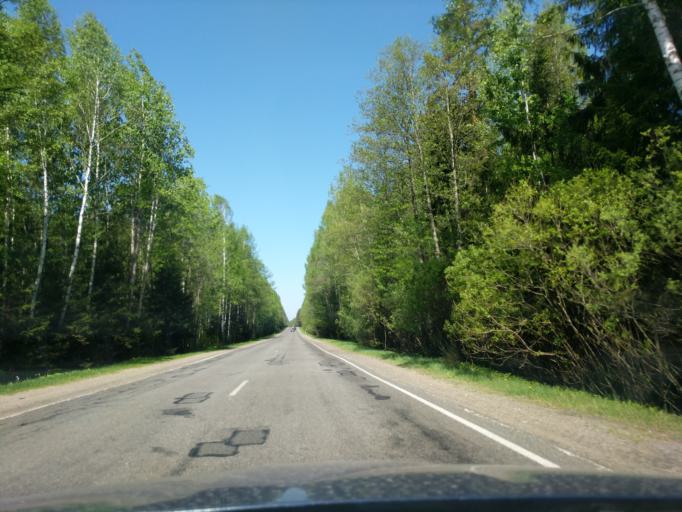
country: BY
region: Minsk
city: Il'ya
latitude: 54.4030
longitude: 27.3231
